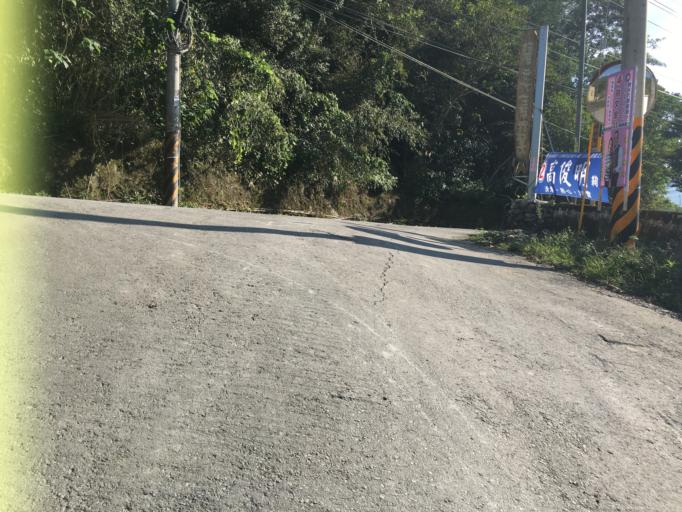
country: TW
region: Taiwan
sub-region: Nantou
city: Puli
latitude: 23.9510
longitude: 121.0755
